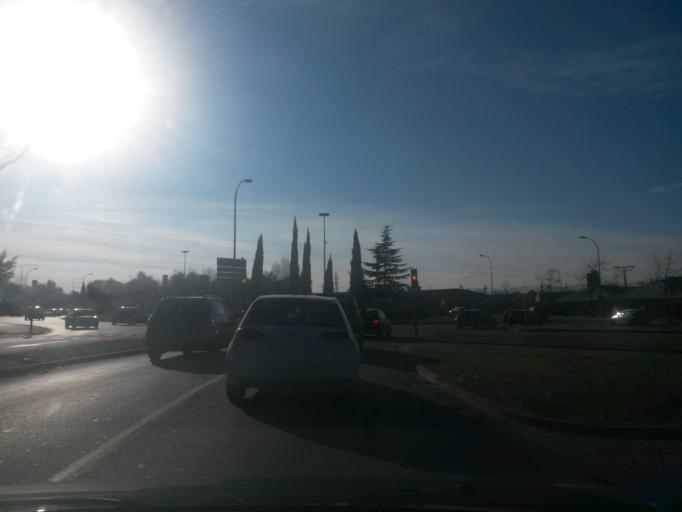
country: ES
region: Catalonia
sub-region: Provincia de Girona
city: Salt
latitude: 41.9617
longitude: 2.8113
